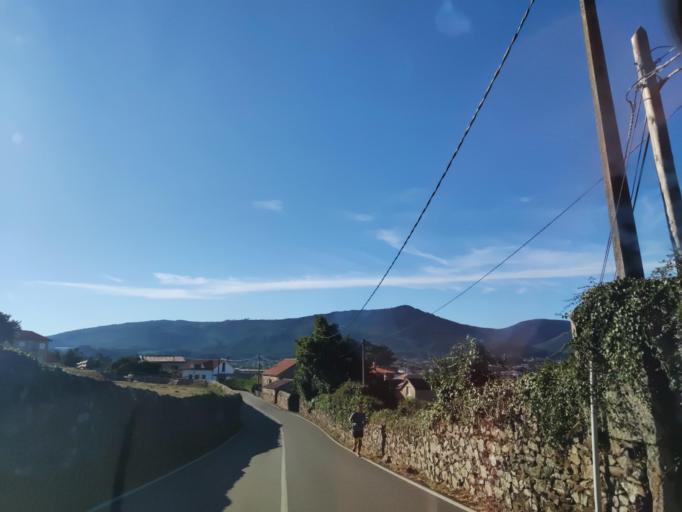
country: ES
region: Galicia
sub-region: Provincia da Coruna
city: Boiro
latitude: 42.5944
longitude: -8.9309
